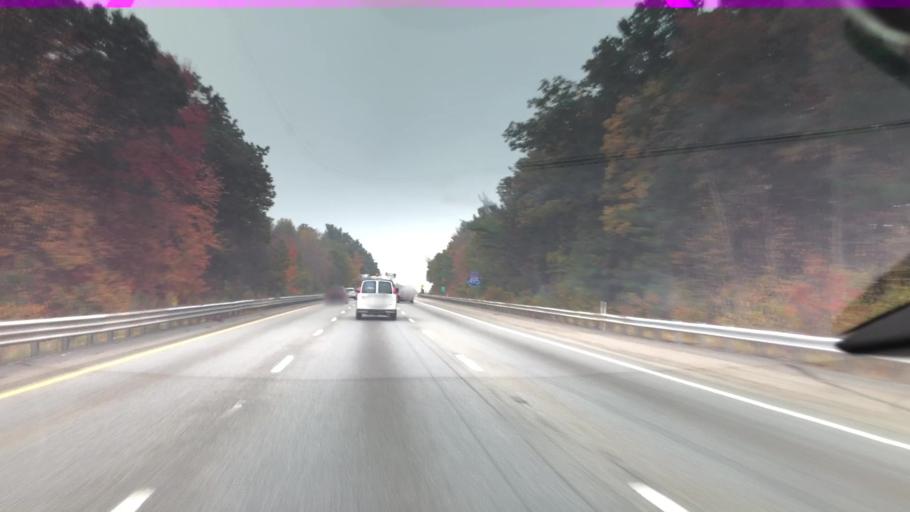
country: US
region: Massachusetts
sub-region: Worcester County
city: Harvard
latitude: 42.4724
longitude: -71.5565
